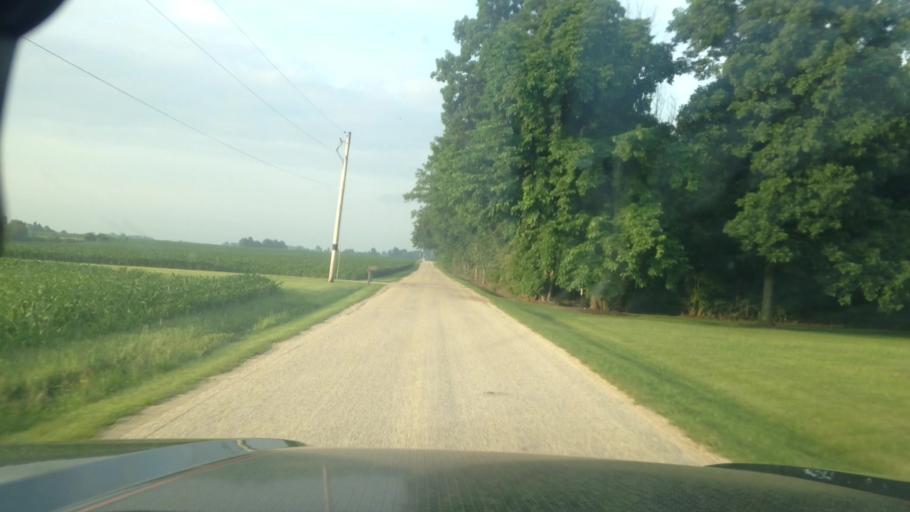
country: US
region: Indiana
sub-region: Randolph County
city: Union City
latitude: 40.2536
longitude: -84.8623
